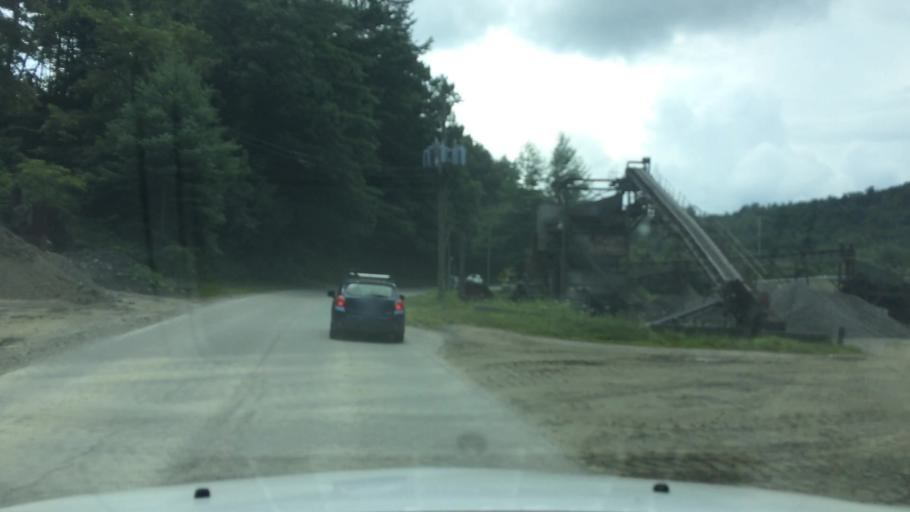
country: US
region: North Carolina
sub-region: Watauga County
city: Boone
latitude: 36.2170
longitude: -81.6369
